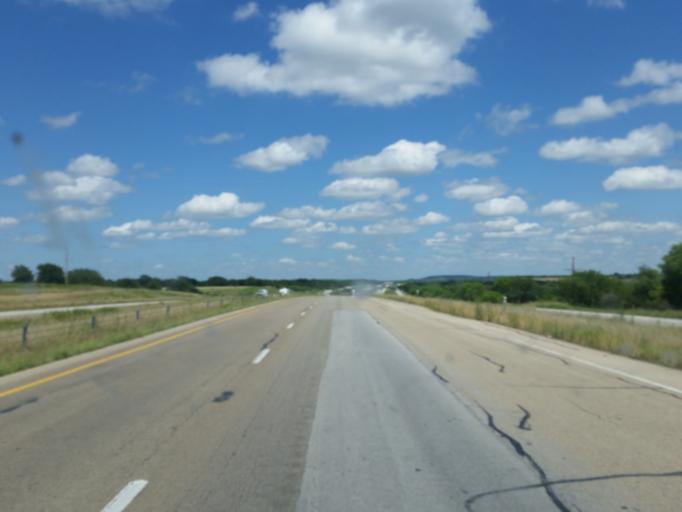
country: US
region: Texas
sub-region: Callahan County
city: Baird
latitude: 32.3852
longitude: -99.2933
